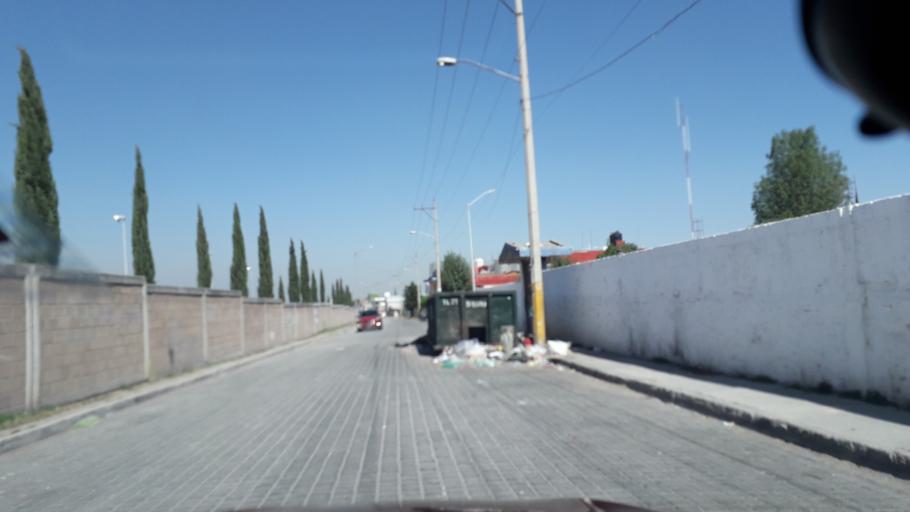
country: MX
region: Puebla
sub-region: Cuautlancingo
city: Sanctorum
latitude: 19.0845
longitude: -98.2153
